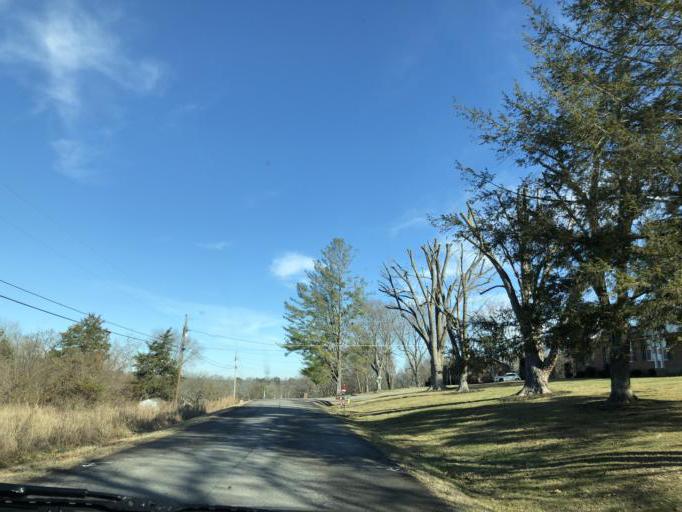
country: US
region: Tennessee
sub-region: Wilson County
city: Mount Juliet
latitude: 36.1779
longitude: -86.5259
